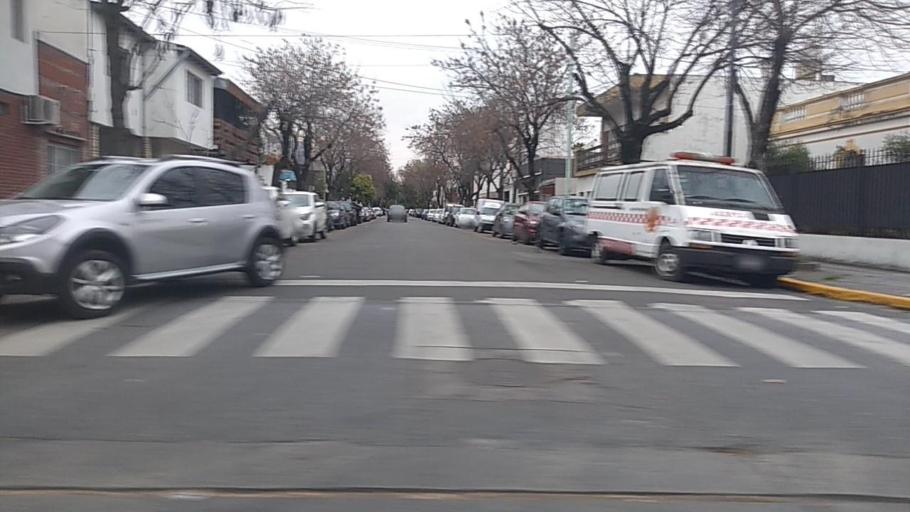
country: AR
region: Buenos Aires F.D.
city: Villa Santa Rita
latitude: -34.6041
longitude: -58.5047
